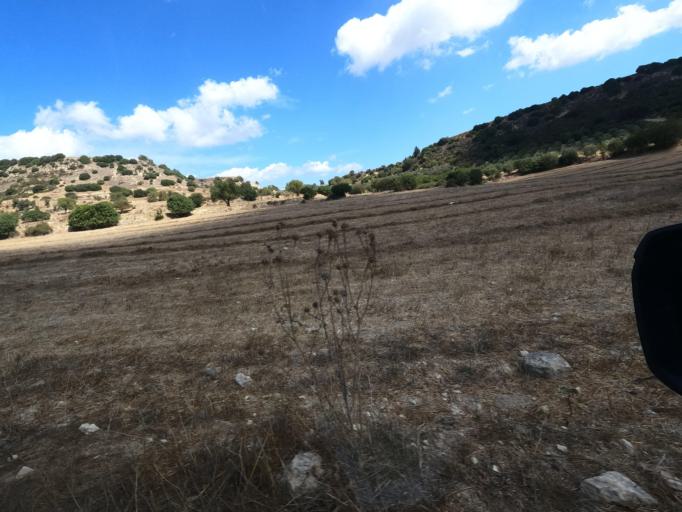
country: CY
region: Pafos
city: Mesogi
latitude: 34.8260
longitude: 32.5508
